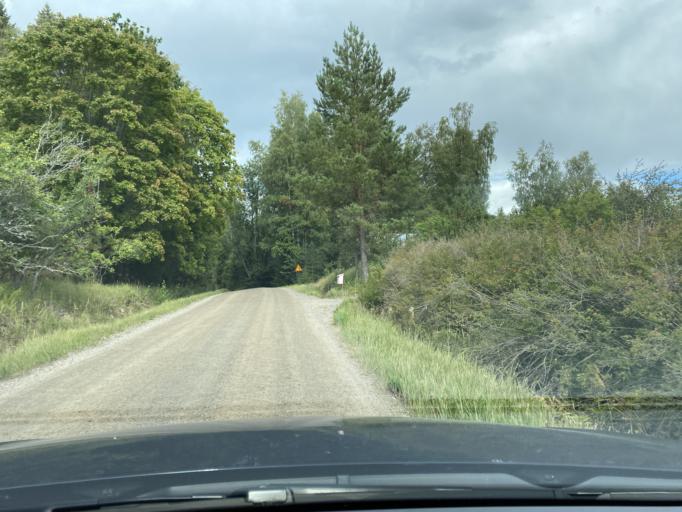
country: FI
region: Haeme
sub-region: Forssa
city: Humppila
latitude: 61.0749
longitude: 23.2742
